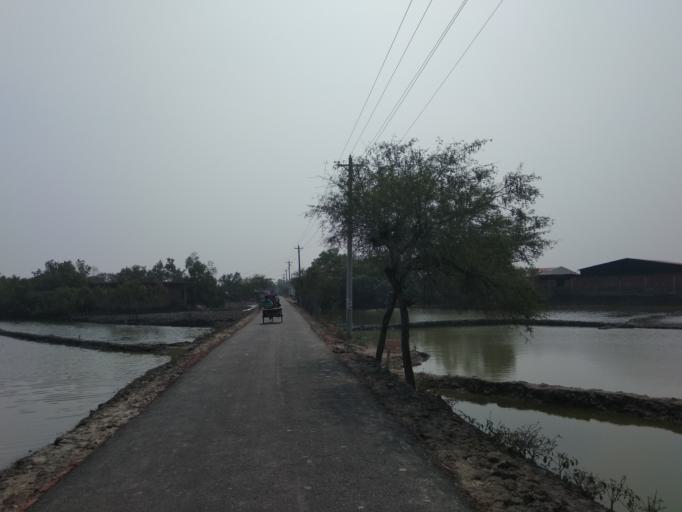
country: IN
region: West Bengal
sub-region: North 24 Parganas
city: Gosaba
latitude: 22.2646
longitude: 89.2197
